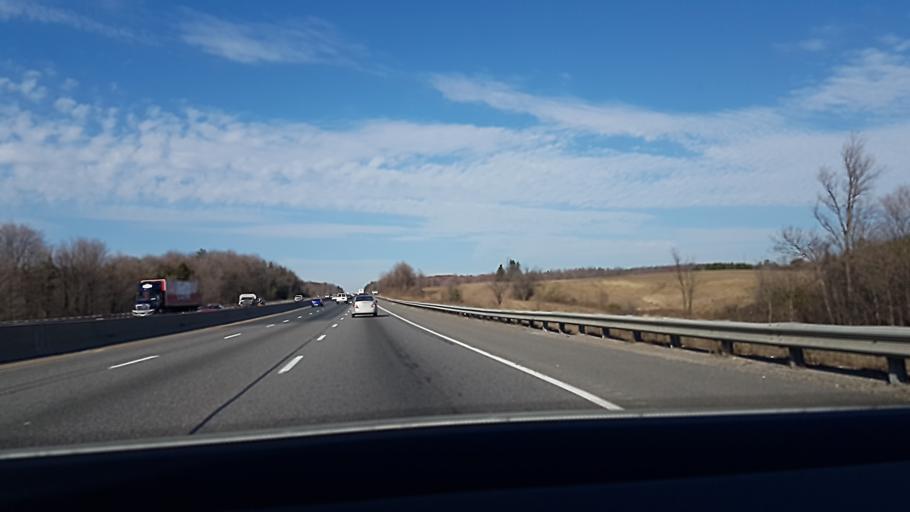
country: CA
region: Ontario
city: Vaughan
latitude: 43.9480
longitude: -79.5725
